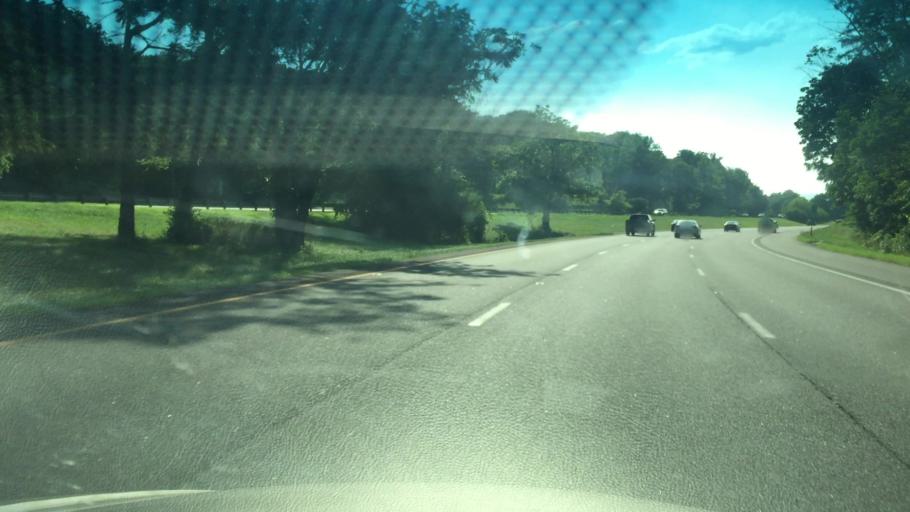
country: US
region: New Jersey
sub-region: Warren County
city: Hackettstown
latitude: 40.9181
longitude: -74.8264
